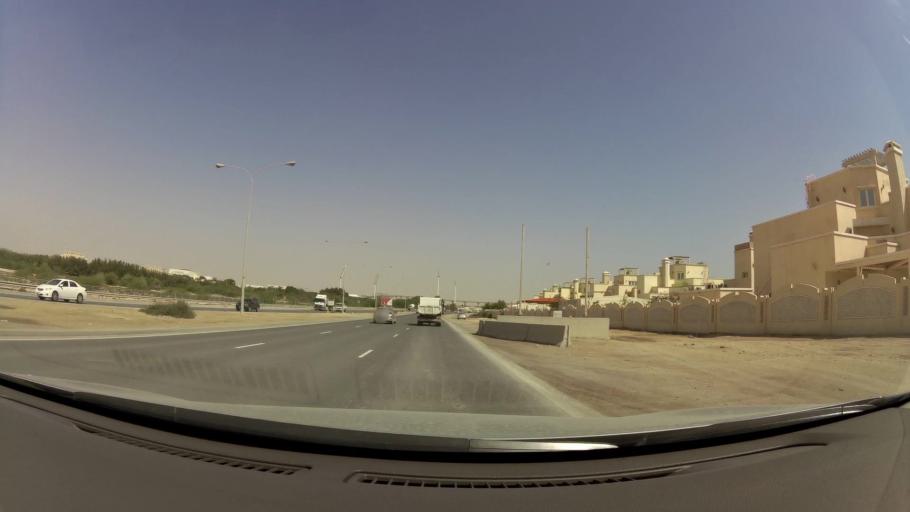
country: QA
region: Baladiyat ad Dawhah
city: Doha
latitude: 25.3698
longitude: 51.4975
